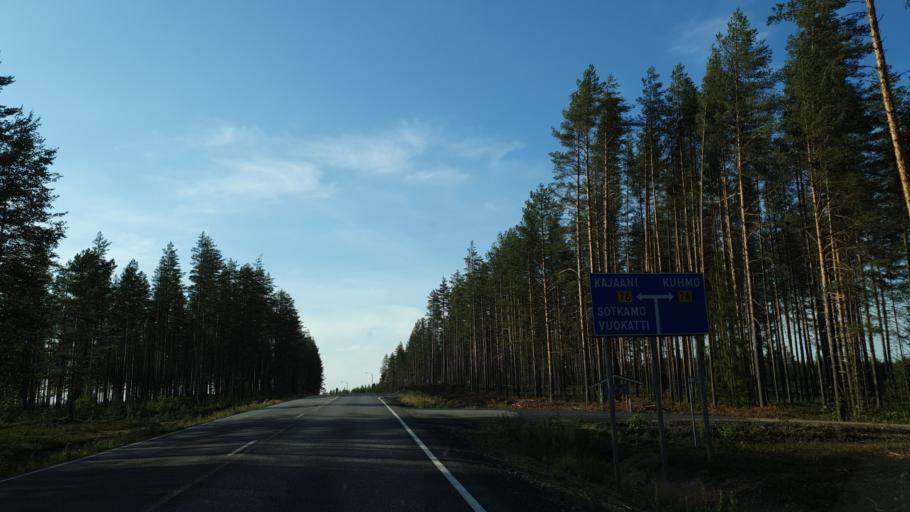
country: FI
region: Kainuu
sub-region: Kehys-Kainuu
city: Kuhmo
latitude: 64.0963
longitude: 29.4768
